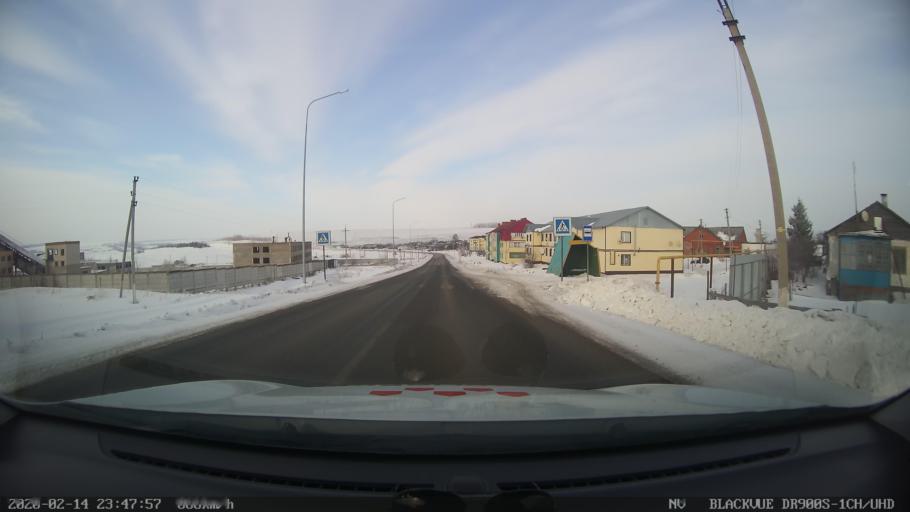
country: RU
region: Tatarstan
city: Kuybyshevskiy Zaton
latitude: 55.2445
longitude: 49.2064
